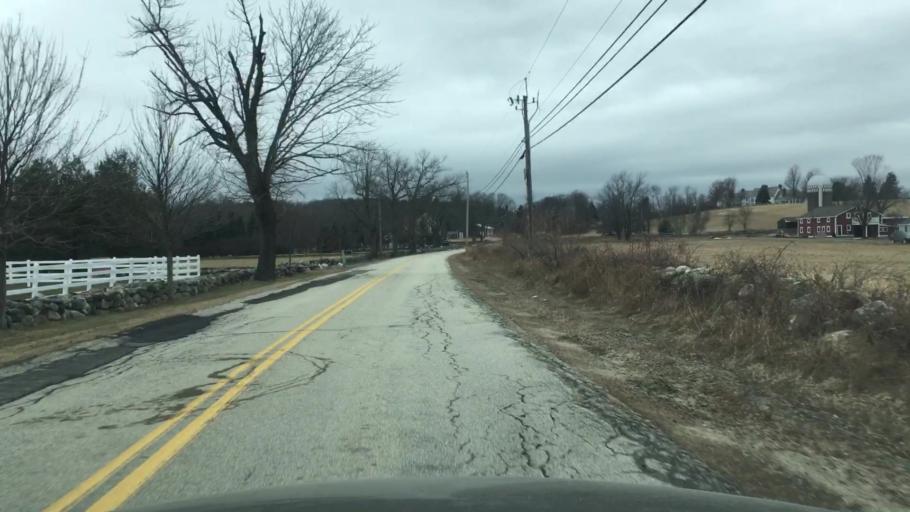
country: US
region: New Hampshire
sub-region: Hillsborough County
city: Mont Vernon
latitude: 42.9291
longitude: -71.6075
